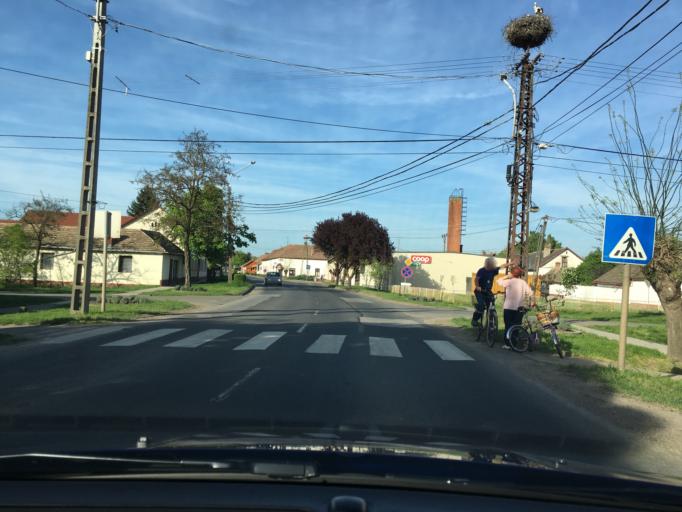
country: HU
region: Bekes
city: Korostarcsa
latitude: 46.8788
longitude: 21.0254
